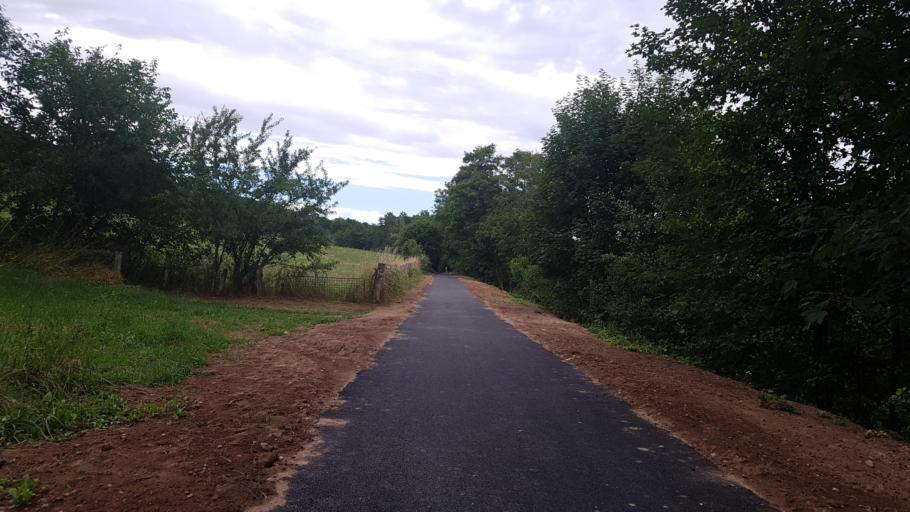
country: FR
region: Lorraine
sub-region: Departement de Meurthe-et-Moselle
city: Chaligny
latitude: 48.6252
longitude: 6.0474
